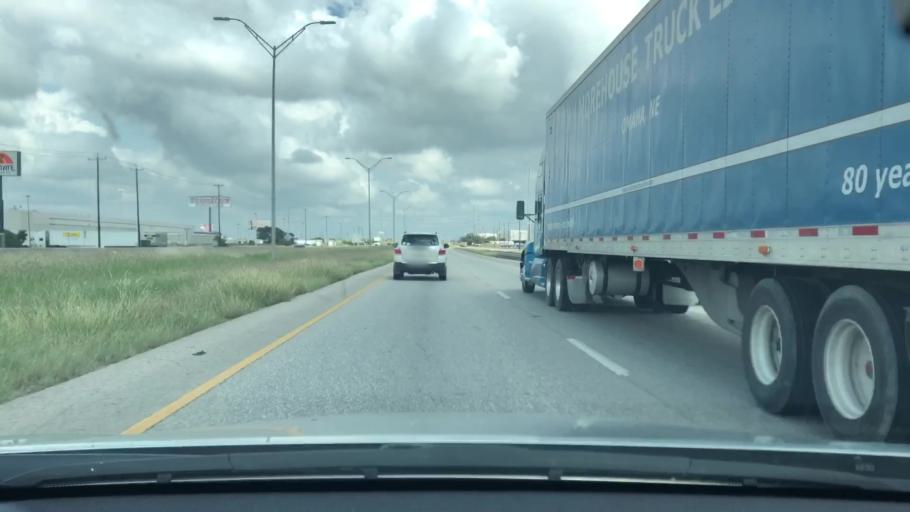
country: US
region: Texas
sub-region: Bexar County
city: Kirby
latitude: 29.4634
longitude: -98.4039
